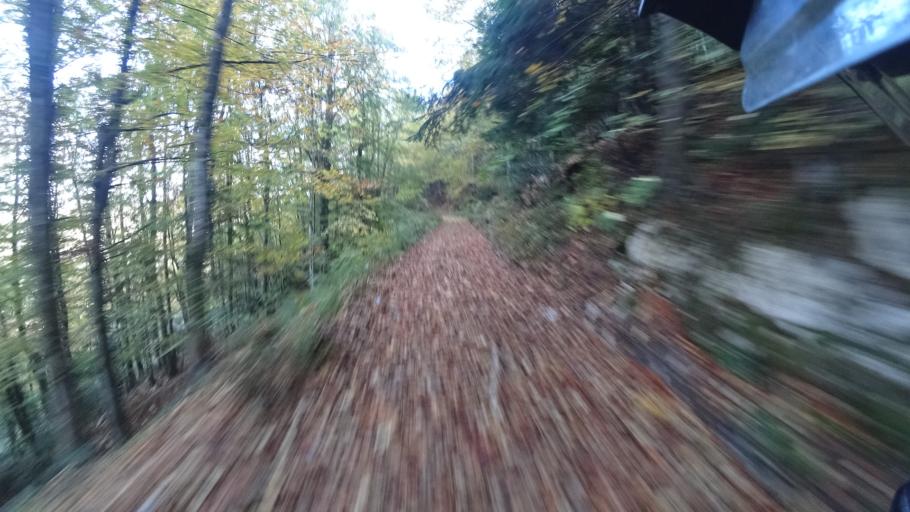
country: HR
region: Karlovacka
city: Plaski
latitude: 44.9621
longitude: 15.4431
